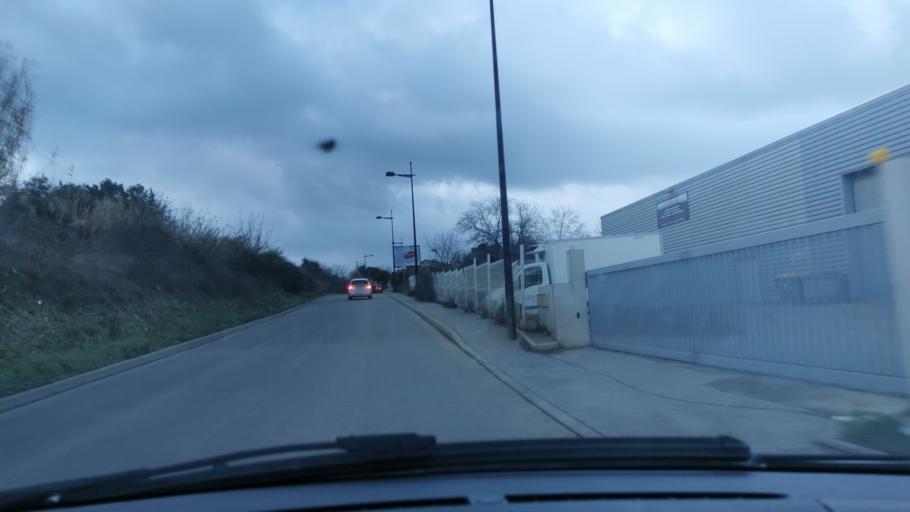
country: FR
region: Languedoc-Roussillon
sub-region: Departement de l'Herault
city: Montpellier
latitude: 43.5856
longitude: 3.8702
